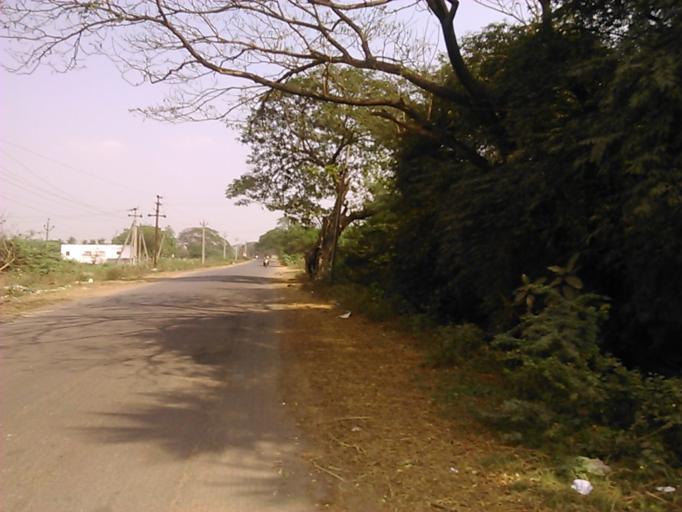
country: IN
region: Andhra Pradesh
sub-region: Guntur
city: Bhattiprolu
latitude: 16.2373
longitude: 80.6674
